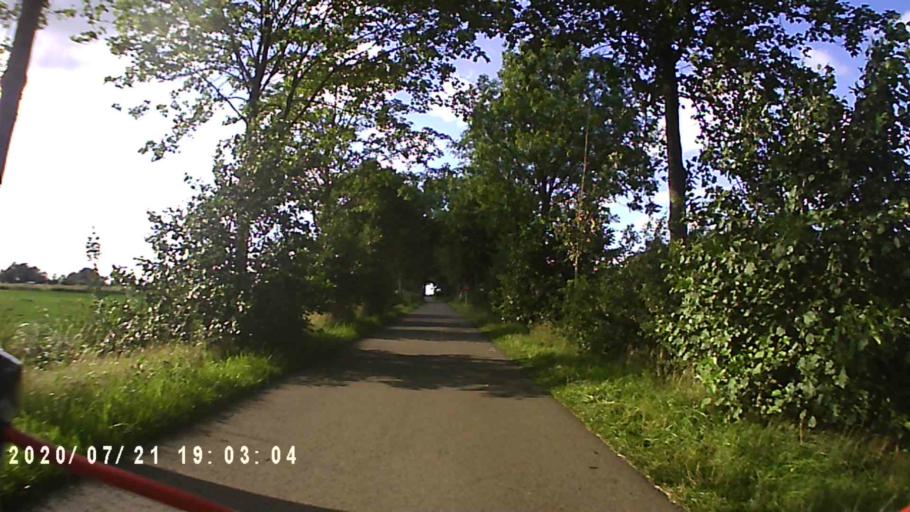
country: NL
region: Groningen
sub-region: Gemeente Slochteren
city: Slochteren
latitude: 53.2329
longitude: 6.7395
